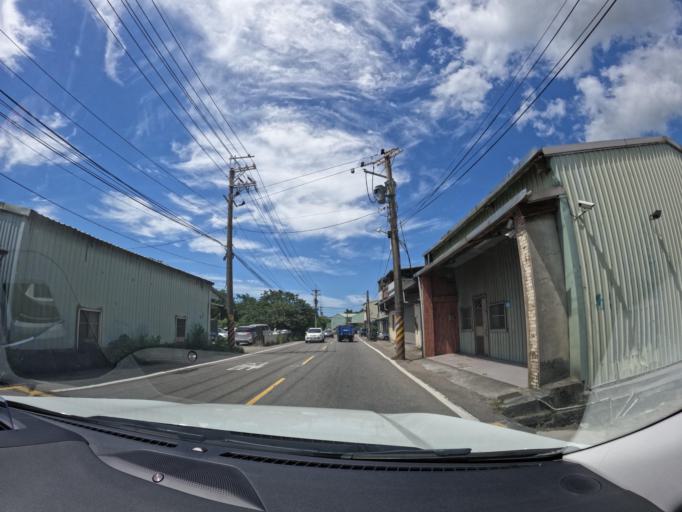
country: TW
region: Taipei
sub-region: Taipei
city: Banqiao
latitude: 25.1289
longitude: 121.3923
